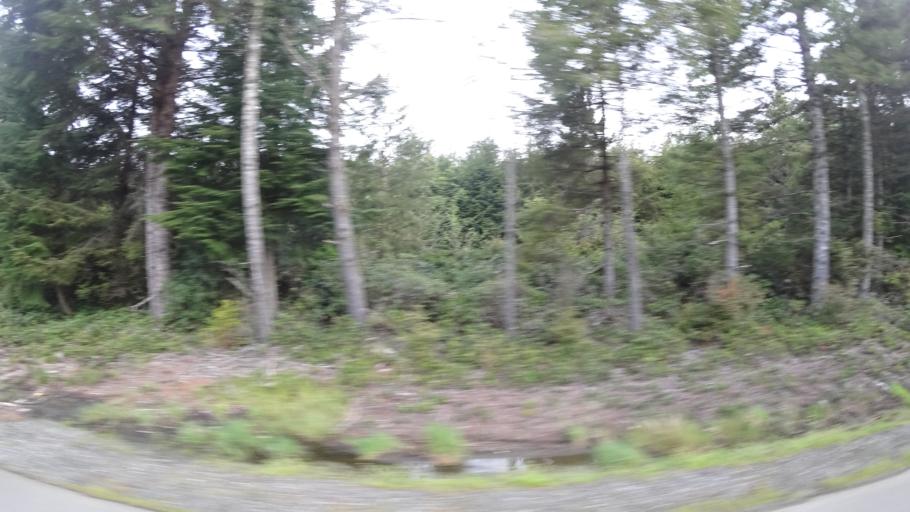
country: US
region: Oregon
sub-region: Coos County
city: Bandon
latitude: 43.1926
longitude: -124.3203
